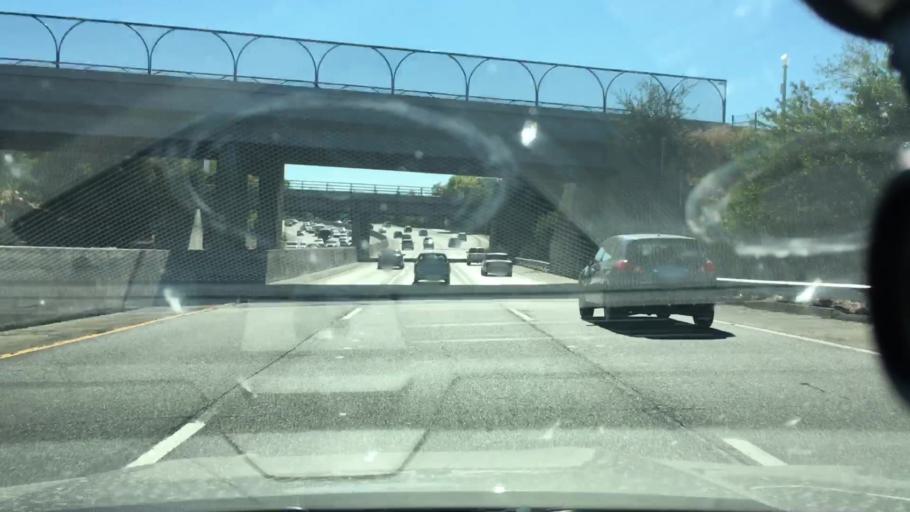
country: US
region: California
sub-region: Sacramento County
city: Sacramento
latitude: 38.5830
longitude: -121.4621
